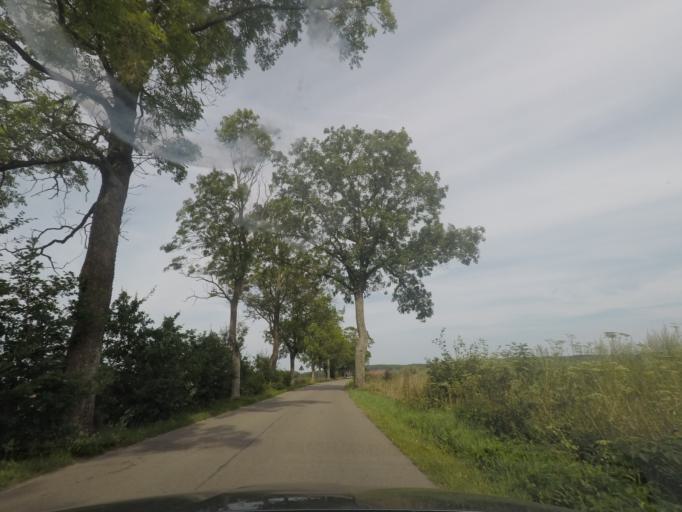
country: PL
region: Pomeranian Voivodeship
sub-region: Slupsk
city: Slupsk
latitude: 54.5948
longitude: 17.0755
